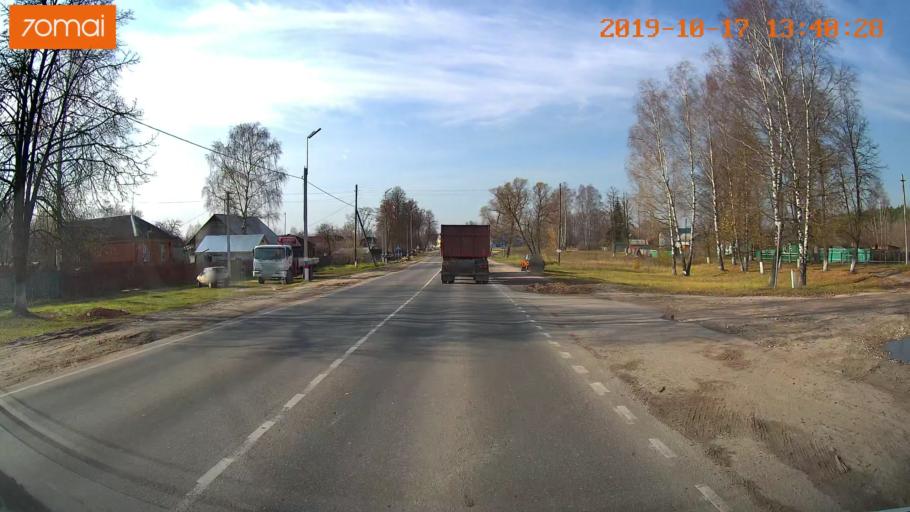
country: RU
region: Rjazan
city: Tuma
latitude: 55.1482
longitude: 40.5730
